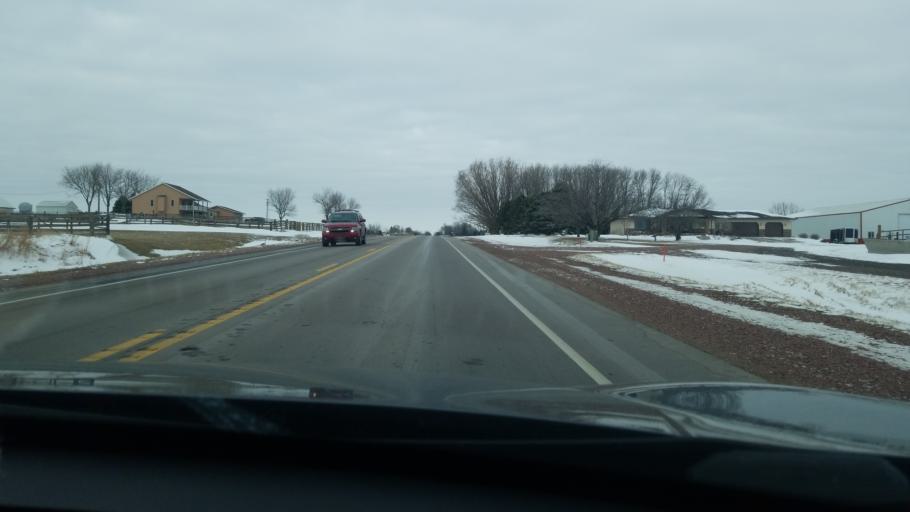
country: US
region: South Dakota
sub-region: Minnehaha County
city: Brandon
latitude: 43.4385
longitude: -96.4292
